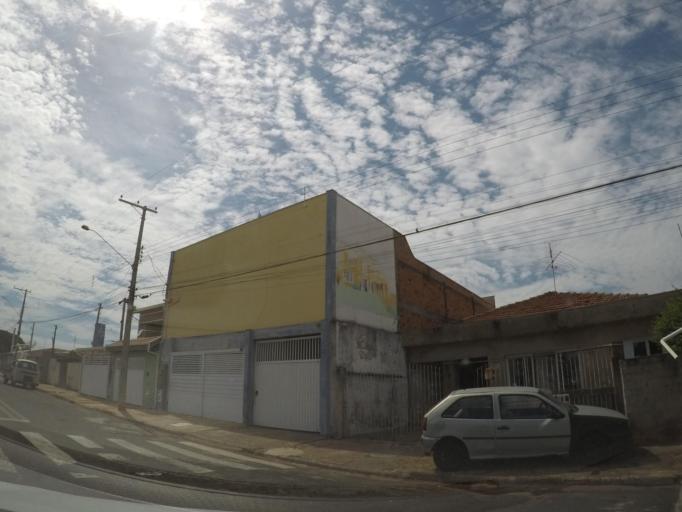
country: BR
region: Sao Paulo
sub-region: Hortolandia
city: Hortolandia
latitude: -22.8343
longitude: -47.1845
